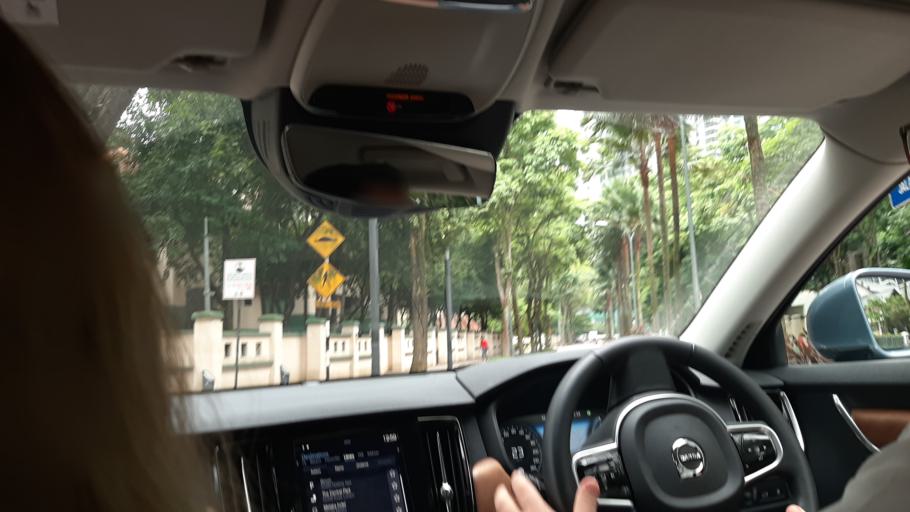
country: MY
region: Kuala Lumpur
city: Kuala Lumpur
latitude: 3.1697
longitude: 101.6529
